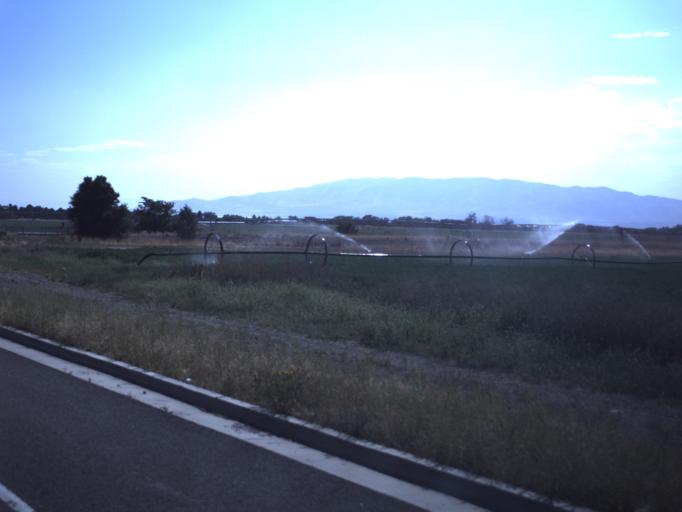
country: US
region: Utah
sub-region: Utah County
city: Cedar Hills
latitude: 40.4088
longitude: -111.7735
